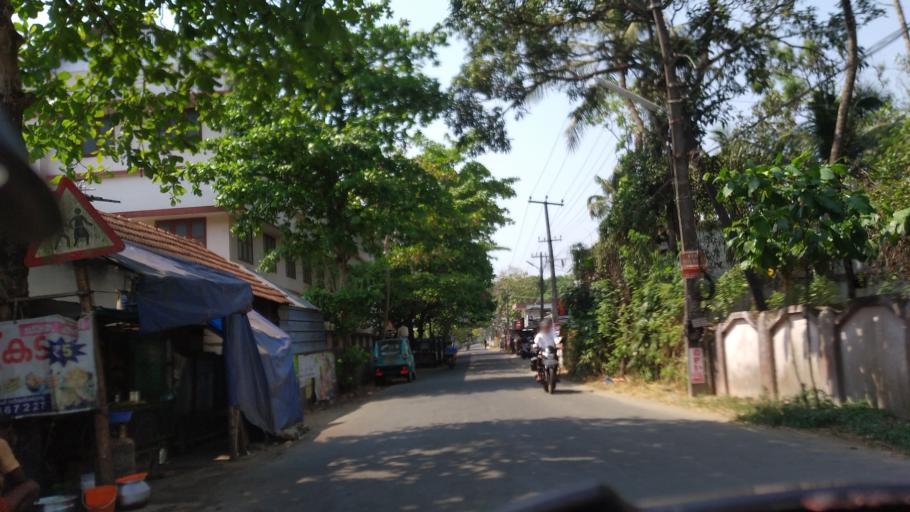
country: IN
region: Kerala
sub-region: Thrissur District
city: Kodungallur
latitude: 10.2484
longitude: 76.1489
